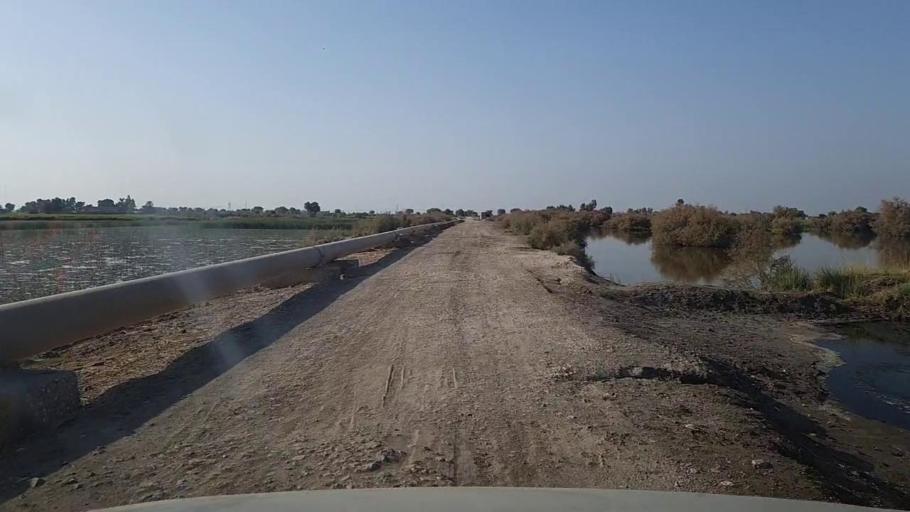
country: PK
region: Sindh
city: Kandhkot
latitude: 28.2830
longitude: 69.3351
